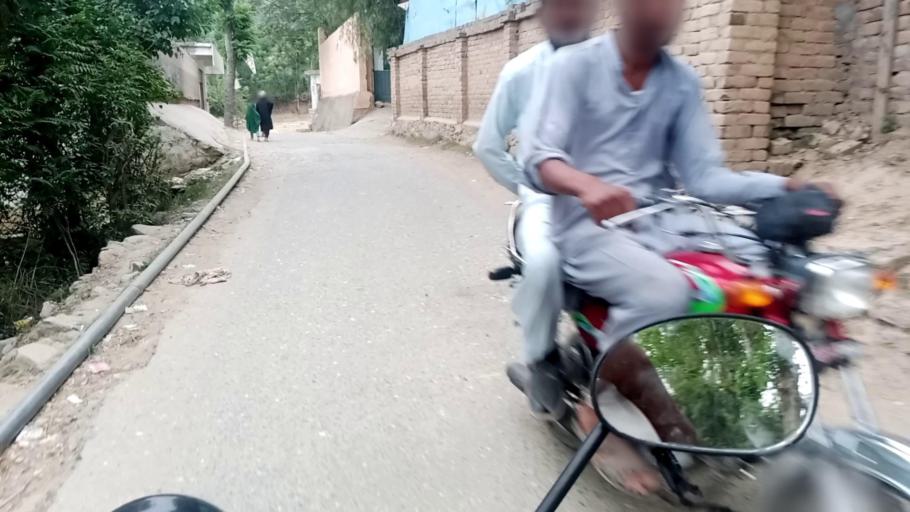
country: PK
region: Khyber Pakhtunkhwa
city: Saidu Sharif
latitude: 34.7516
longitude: 72.3778
